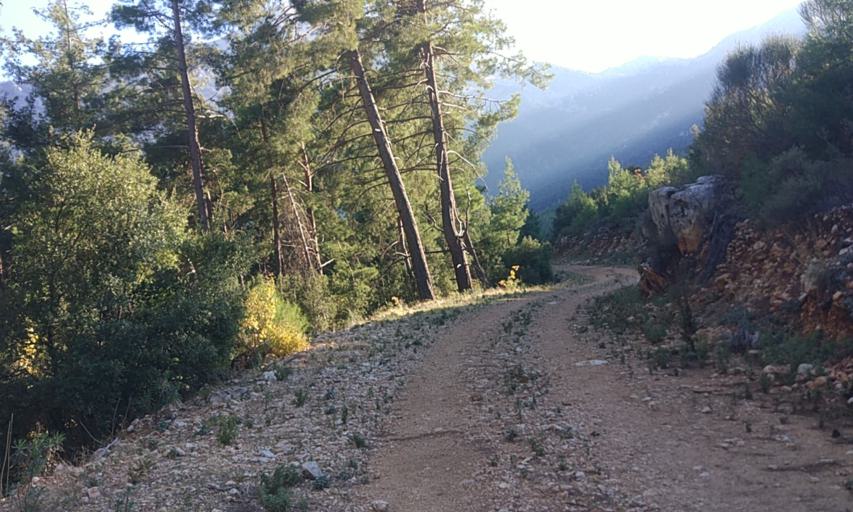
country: TR
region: Antalya
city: Altinyaka
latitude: 36.5915
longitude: 30.4269
